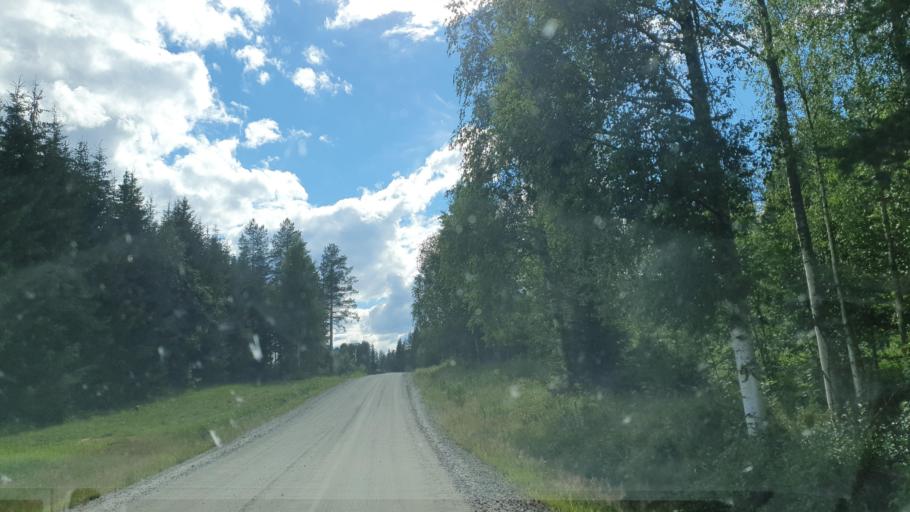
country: FI
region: Kainuu
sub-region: Kehys-Kainuu
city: Kuhmo
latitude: 64.1300
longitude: 29.6505
